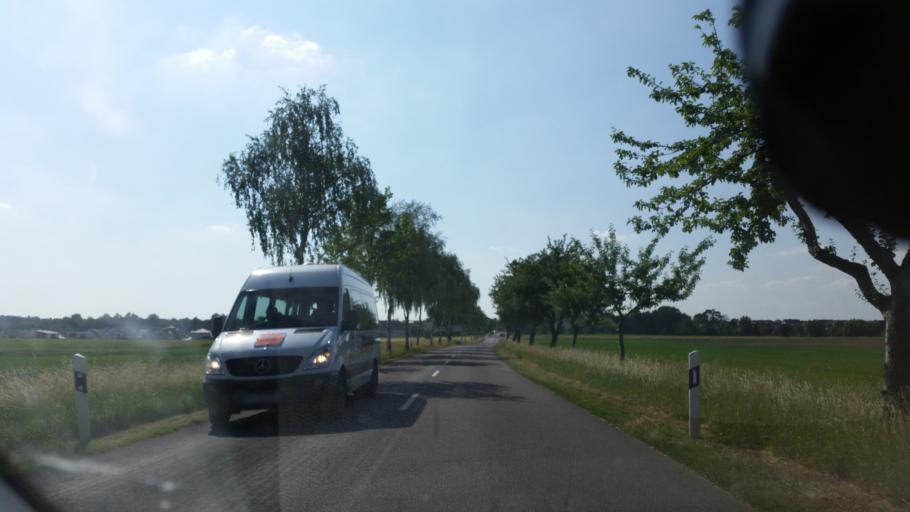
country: DE
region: Lower Saxony
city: Lehre
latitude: 52.3221
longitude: 10.6808
